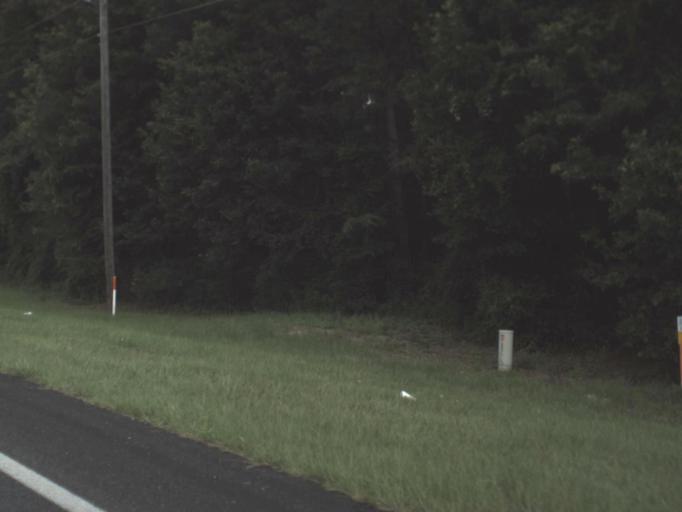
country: US
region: Florida
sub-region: Levy County
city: Williston
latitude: 29.4018
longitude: -82.5090
